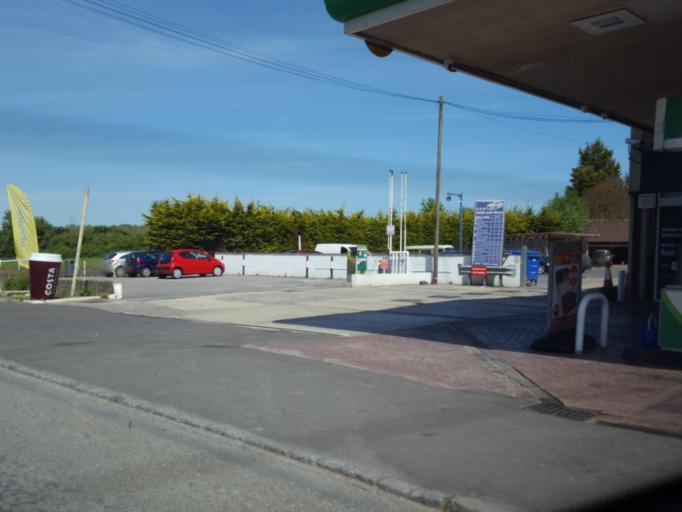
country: GB
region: England
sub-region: Wiltshire
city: Malmesbury
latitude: 51.5916
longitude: -2.0891
